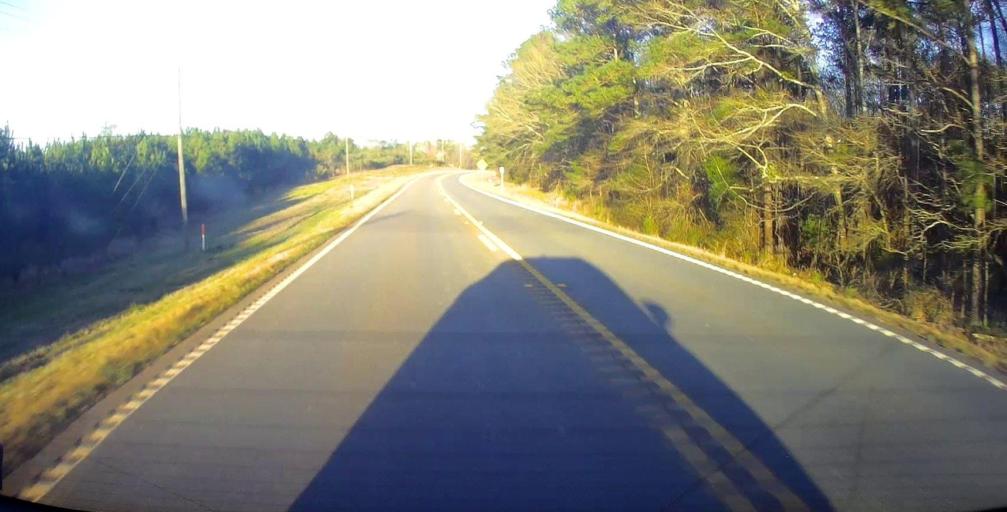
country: US
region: Georgia
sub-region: Harris County
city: Hamilton
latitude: 32.6729
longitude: -84.9428
